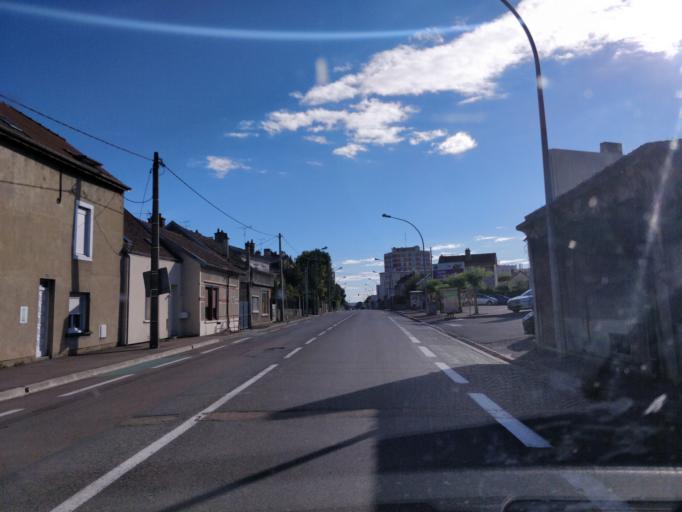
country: FR
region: Champagne-Ardenne
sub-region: Departement de l'Aube
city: Troyes
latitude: 48.2839
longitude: 4.0725
